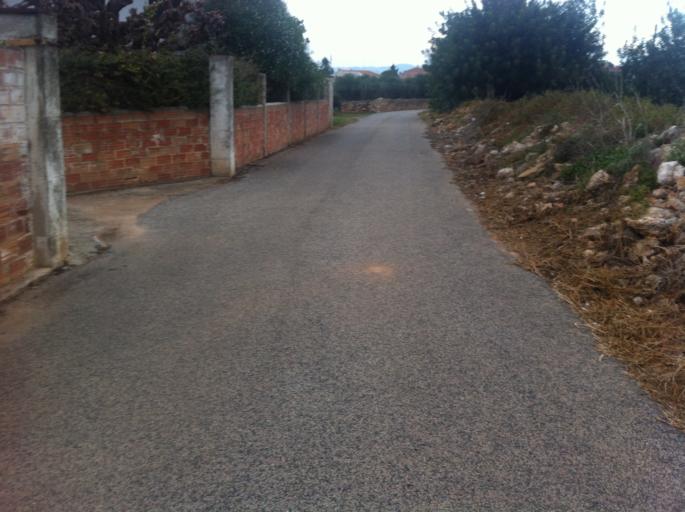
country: ES
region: Catalonia
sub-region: Provincia de Tarragona
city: Santa Oliva
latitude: 41.2482
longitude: 1.5480
